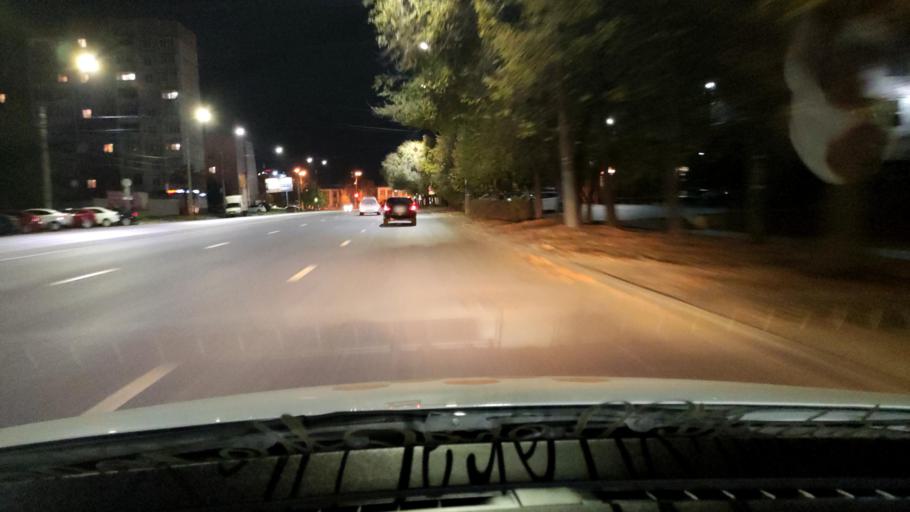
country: RU
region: Voronezj
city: Voronezh
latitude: 51.6723
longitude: 39.1637
